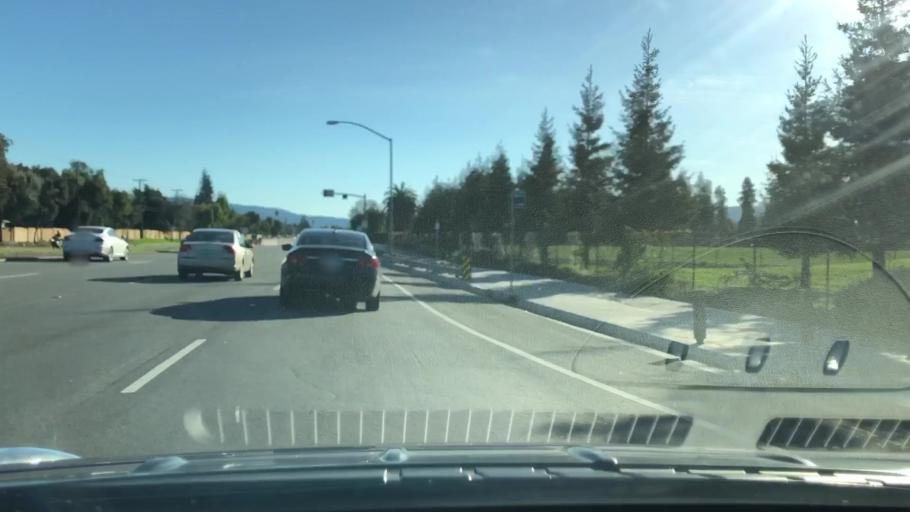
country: US
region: California
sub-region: Santa Clara County
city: Santa Clara
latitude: 37.3587
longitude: -121.9692
